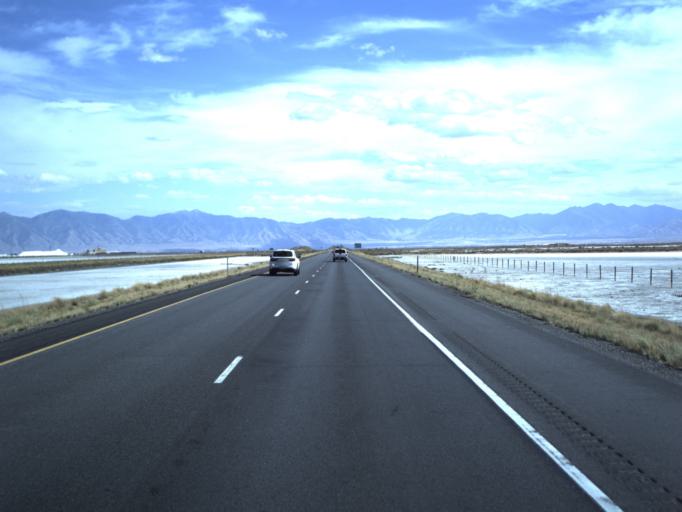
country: US
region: Utah
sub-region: Tooele County
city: Grantsville
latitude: 40.7175
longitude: -112.5492
